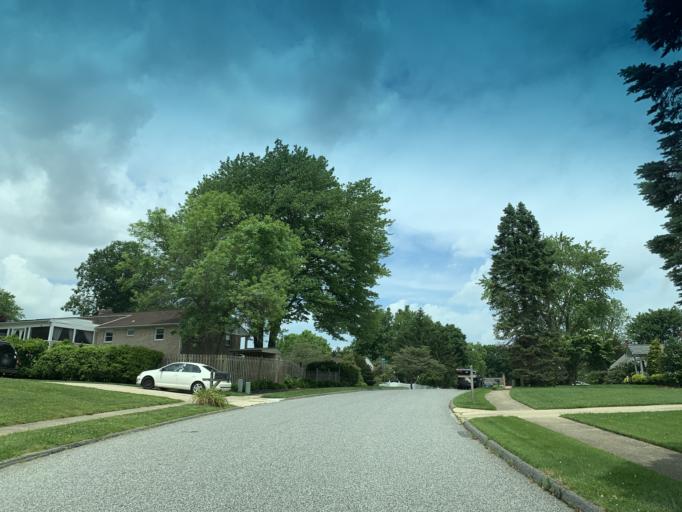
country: US
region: Maryland
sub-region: Harford County
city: South Bel Air
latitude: 39.5395
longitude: -76.3020
